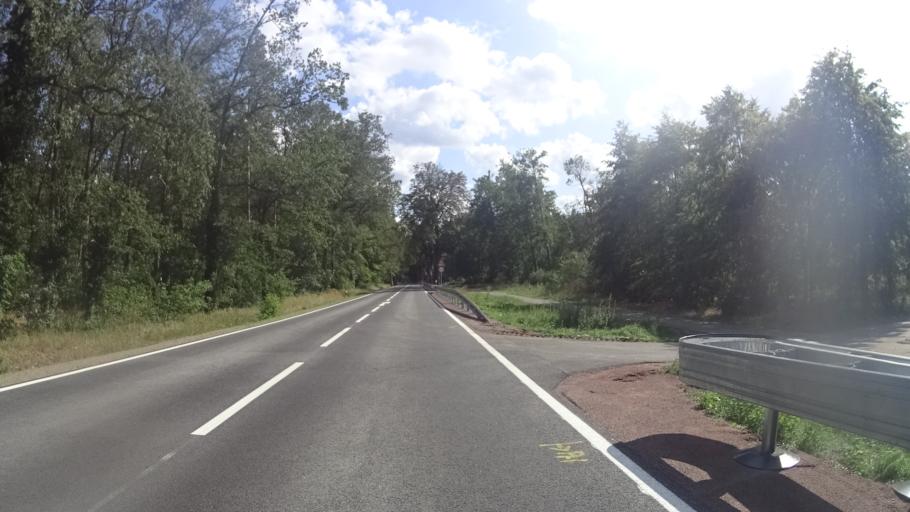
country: DE
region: Brandenburg
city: Rhinow
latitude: 52.7414
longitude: 12.3367
